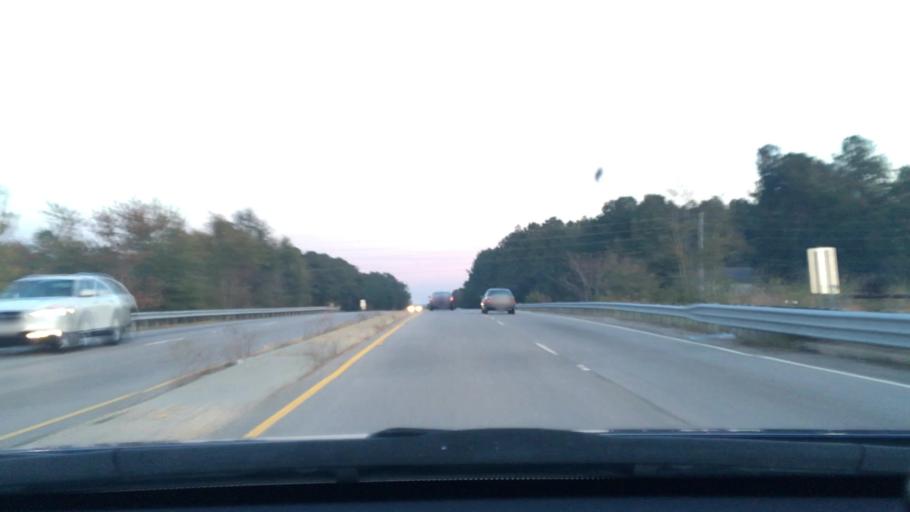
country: US
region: South Carolina
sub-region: Richland County
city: Gadsden
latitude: 33.9426
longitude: -80.6870
